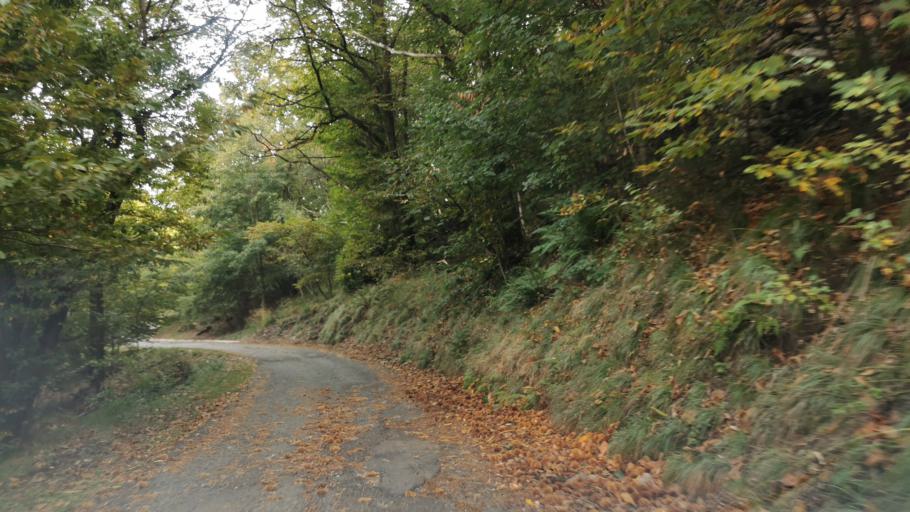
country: IT
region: Lombardy
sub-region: Provincia di Como
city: San Siro
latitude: 46.0771
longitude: 9.2557
